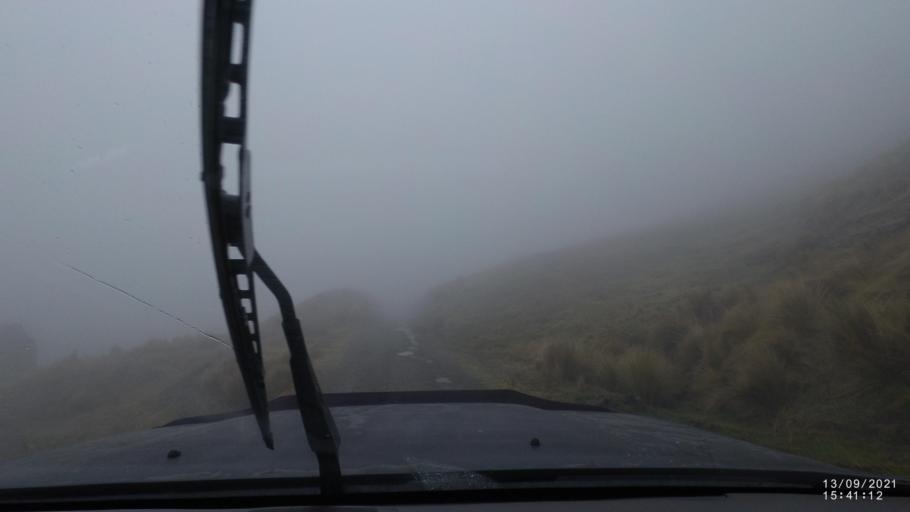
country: BO
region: Cochabamba
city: Colomi
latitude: -17.3238
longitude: -65.7178
